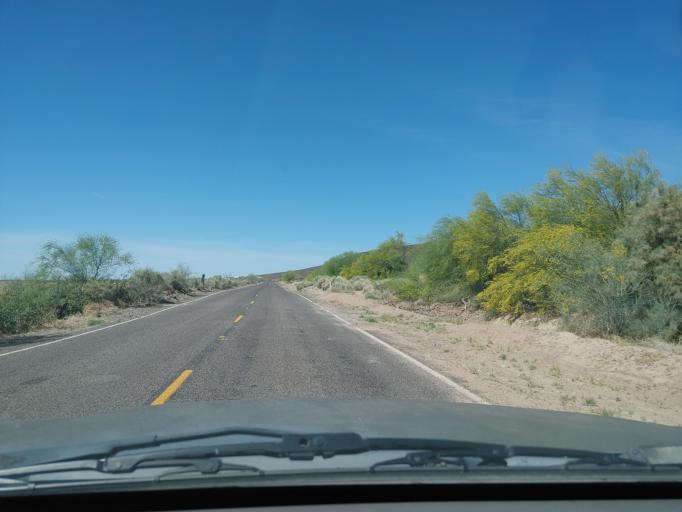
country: US
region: Arizona
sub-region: Maricopa County
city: Gila Bend
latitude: 32.9863
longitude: -113.3143
